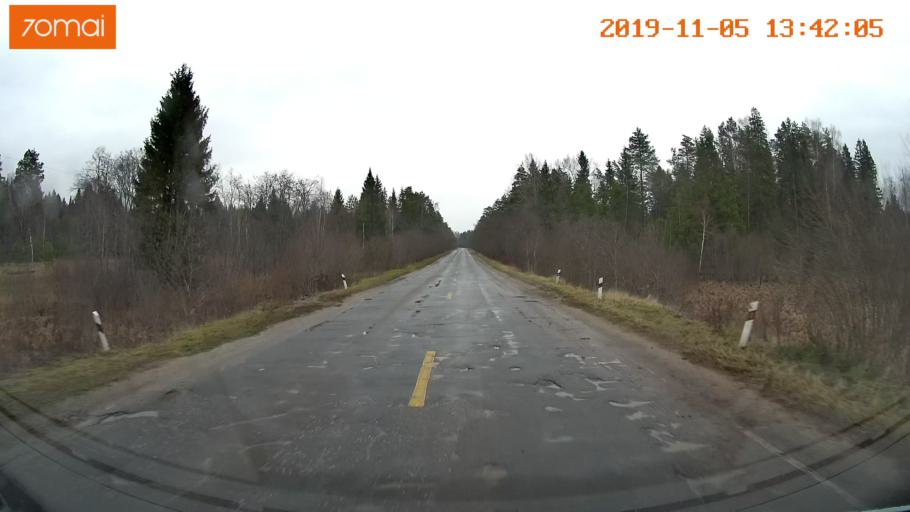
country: RU
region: Ivanovo
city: Shuya
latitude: 56.9643
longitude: 41.3899
